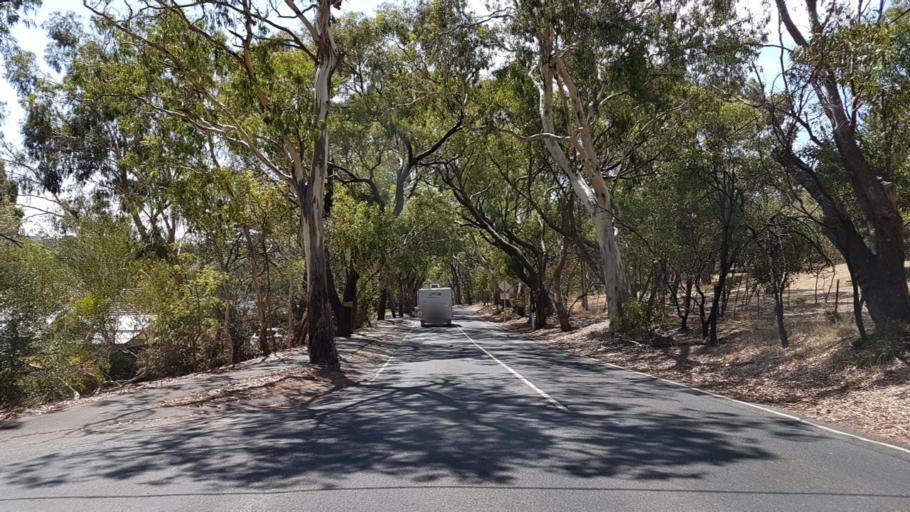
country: AU
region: South Australia
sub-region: Mitcham
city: Belair
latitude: -35.0135
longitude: 138.6335
